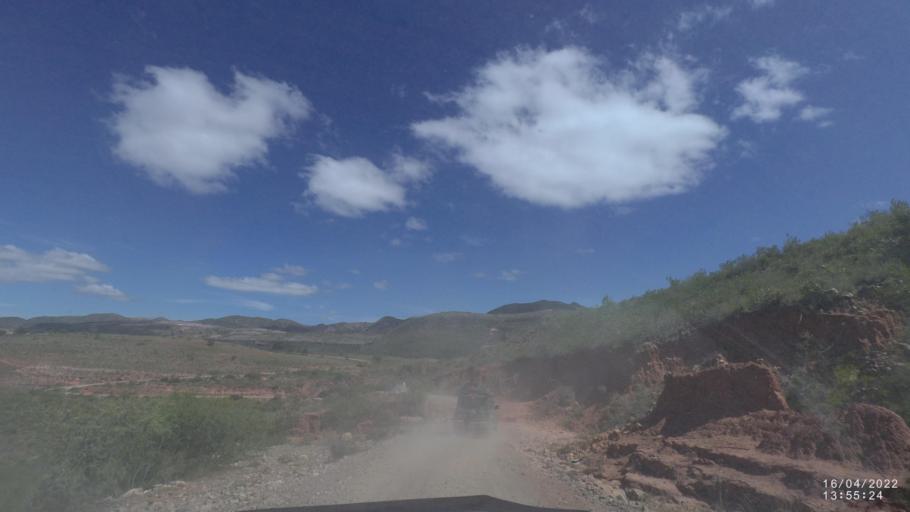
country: BO
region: Cochabamba
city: Mizque
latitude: -18.0286
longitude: -65.5647
